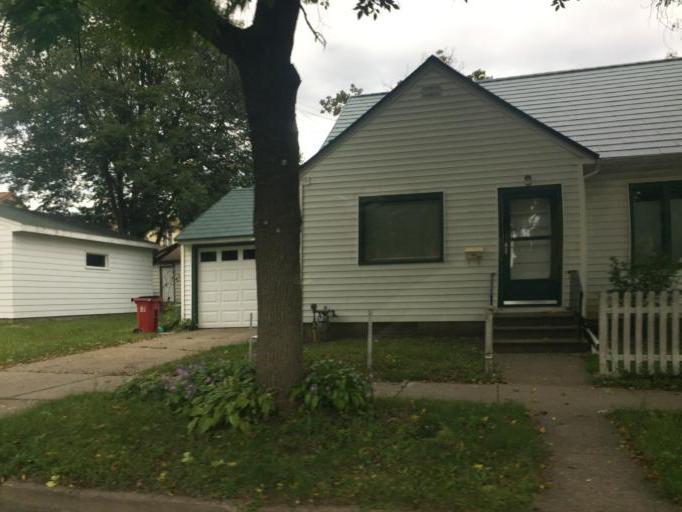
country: US
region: Minnesota
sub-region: Winona County
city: Winona
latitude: 44.0498
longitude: -91.6613
